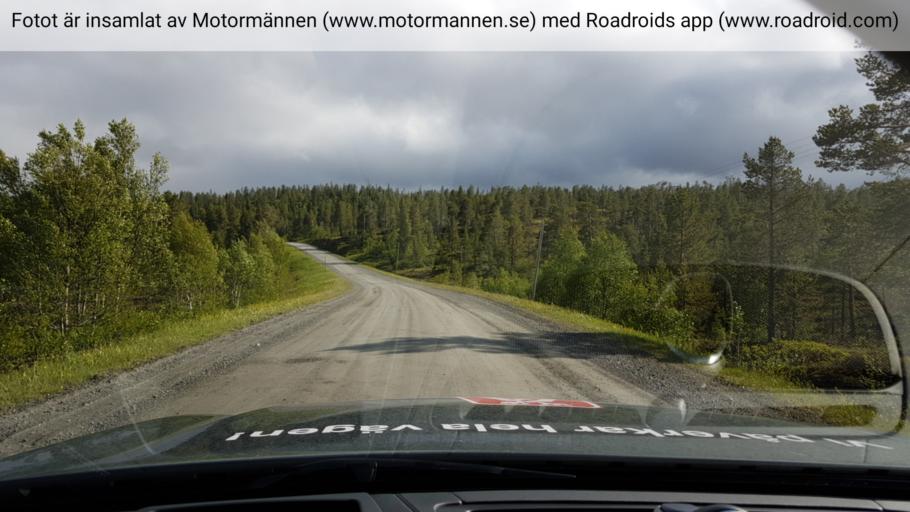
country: NO
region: Nord-Trondelag
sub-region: Snasa
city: Snaase
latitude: 63.7252
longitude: 12.4764
